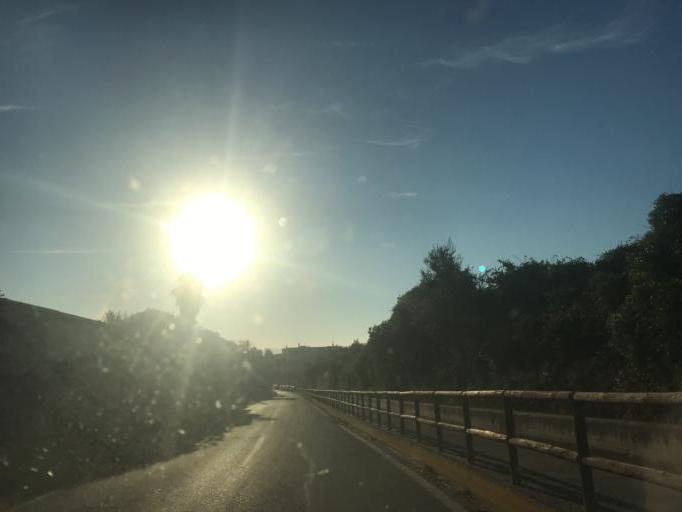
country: IT
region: Sardinia
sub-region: Provincia di Sassari
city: Alghero
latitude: 40.5547
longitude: 8.3325
